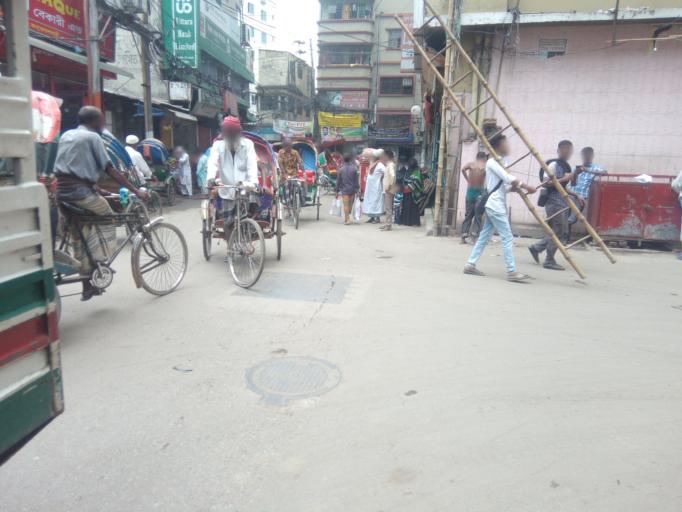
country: BD
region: Dhaka
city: Azimpur
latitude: 23.7173
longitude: 90.3900
